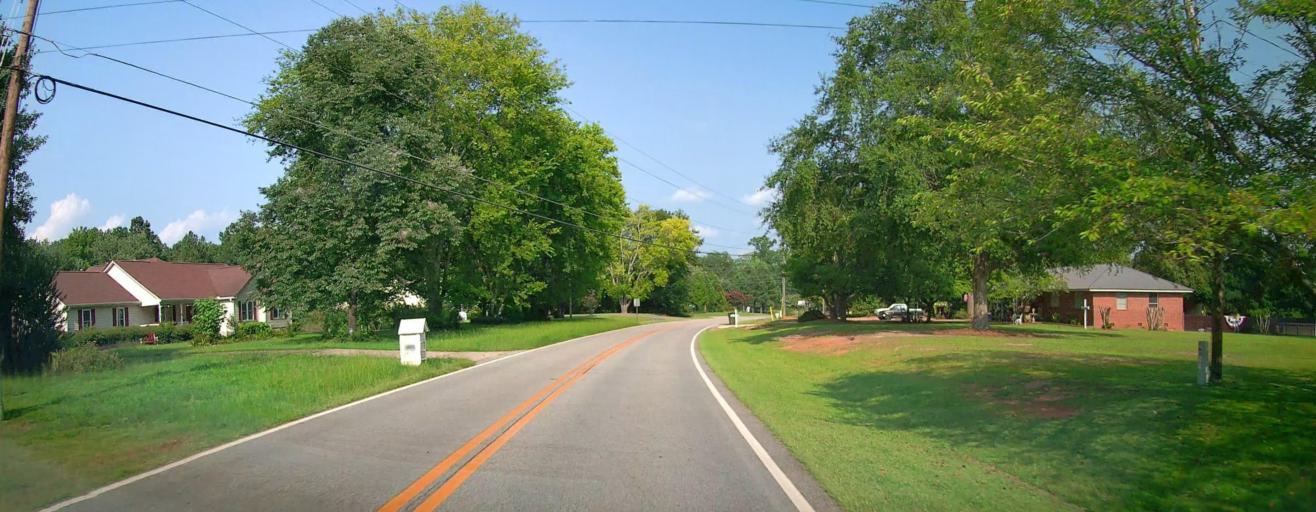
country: US
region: Georgia
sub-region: Houston County
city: Centerville
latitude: 32.7322
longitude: -83.6832
